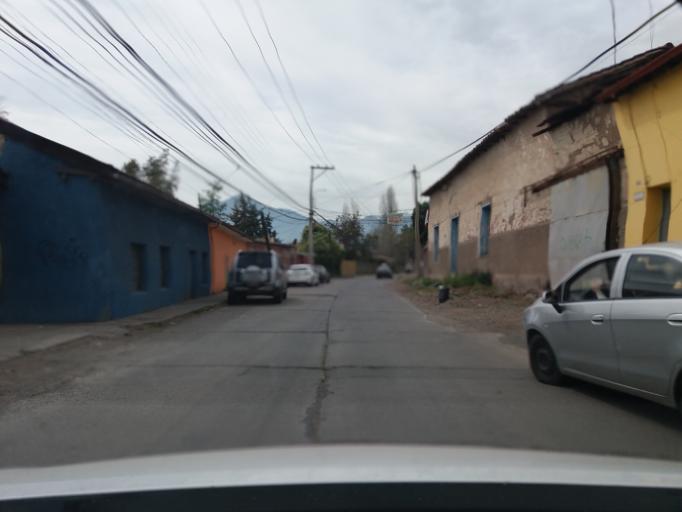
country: CL
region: Valparaiso
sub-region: Provincia de Los Andes
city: Los Andes
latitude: -32.8346
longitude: -70.5893
